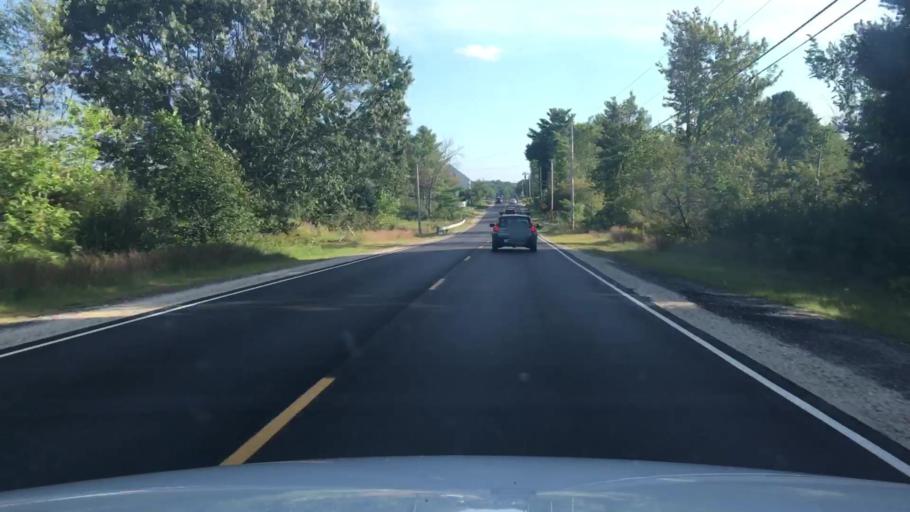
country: US
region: Maine
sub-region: Cumberland County
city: Cumberland Center
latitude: 43.7902
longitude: -70.3053
